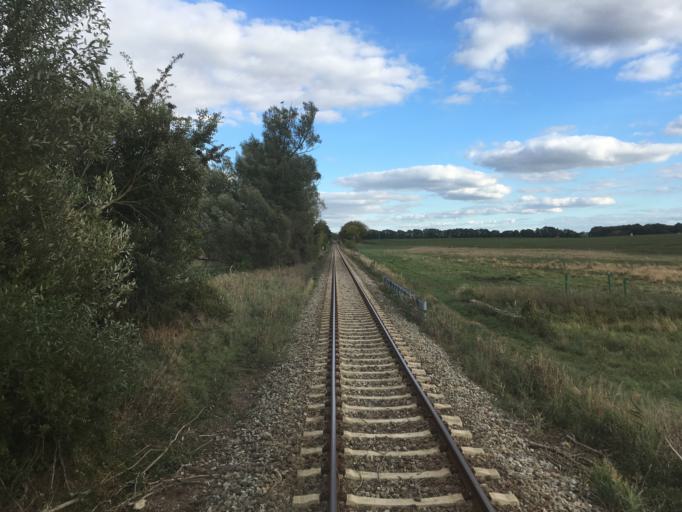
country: DE
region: Mecklenburg-Vorpommern
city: Grabowhofe
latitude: 53.5411
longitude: 12.5926
